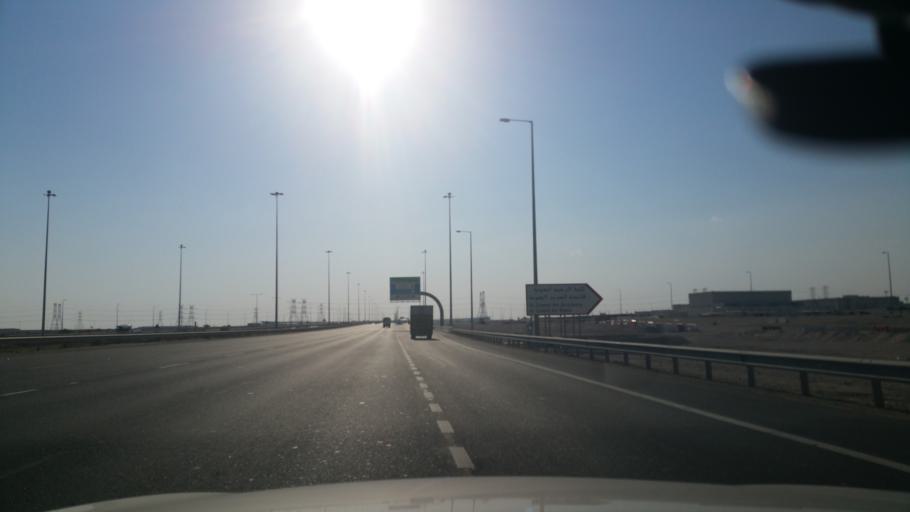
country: QA
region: Baladiyat ar Rayyan
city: Ar Rayyan
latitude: 25.1798
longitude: 51.3484
